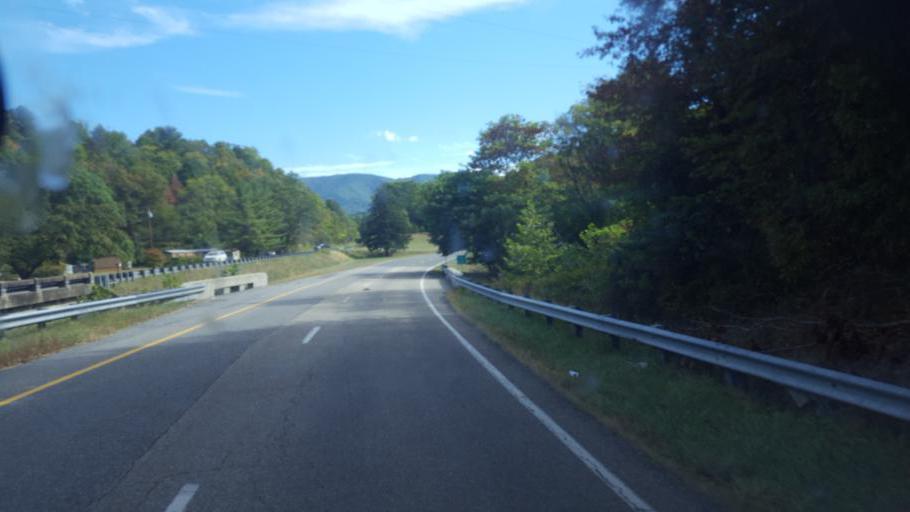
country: US
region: Virginia
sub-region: Page County
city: Luray
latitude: 38.6709
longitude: -78.3815
